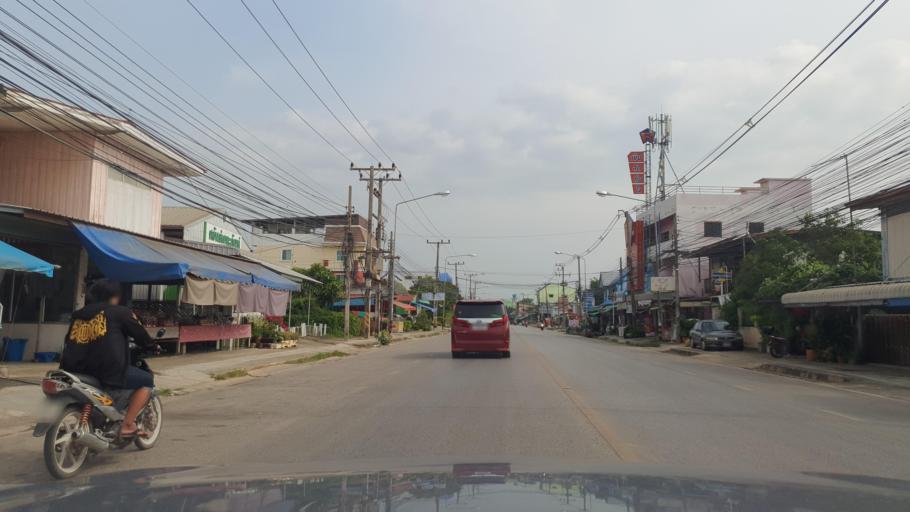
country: TH
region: Phitsanulok
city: Phitsanulok
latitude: 16.8509
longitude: 100.2548
